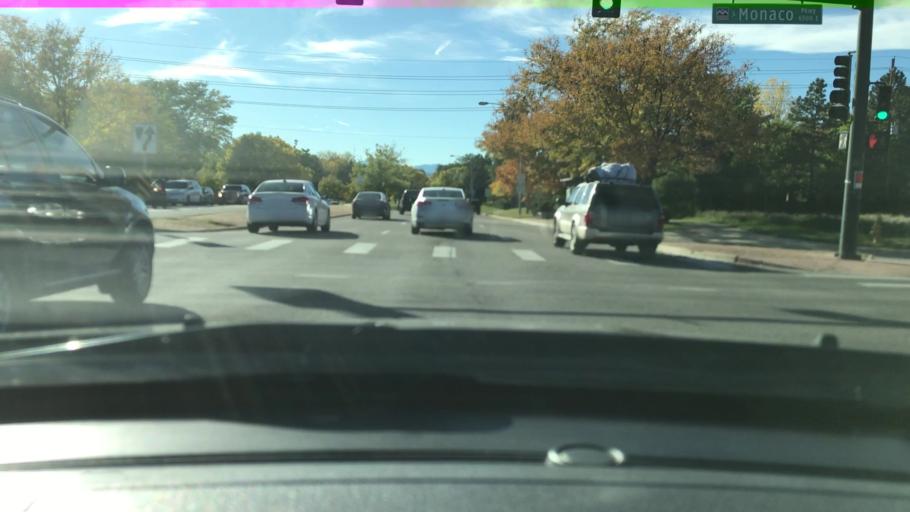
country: US
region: Colorado
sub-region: Arapahoe County
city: Glendale
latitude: 39.7114
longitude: -104.9133
